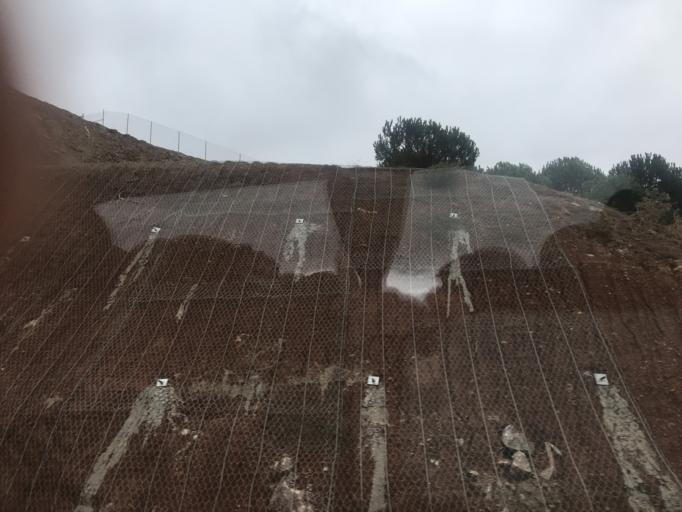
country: TR
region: Balikesir
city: Yenikoy
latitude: 39.7983
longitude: 28.0385
